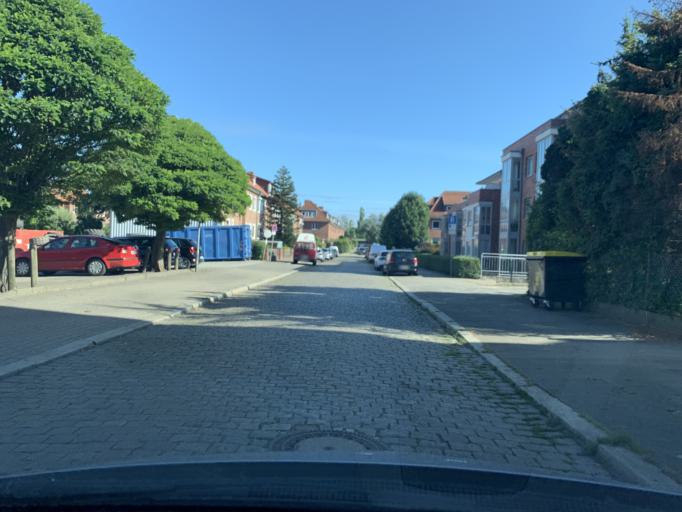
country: DE
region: Lower Saxony
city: Lueneburg
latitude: 53.2512
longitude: 10.4247
